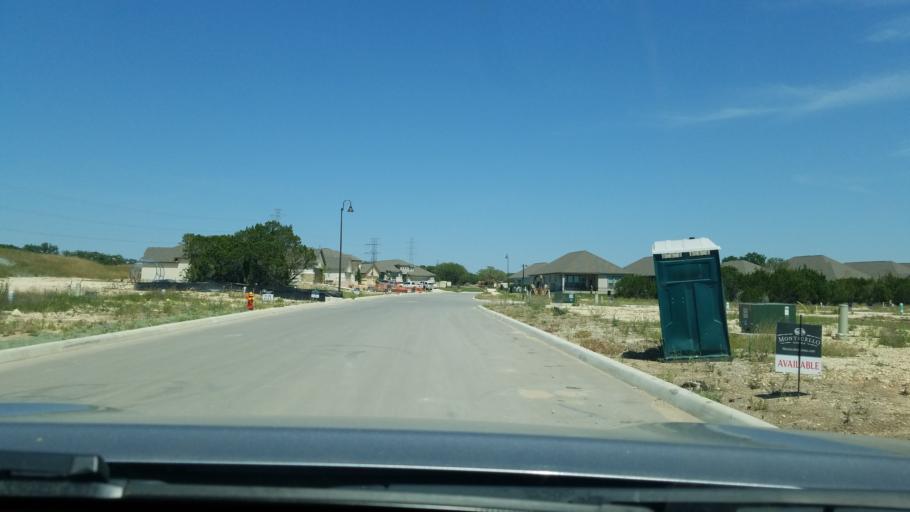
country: US
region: Texas
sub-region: Kendall County
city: Boerne
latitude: 29.8034
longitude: -98.6960
